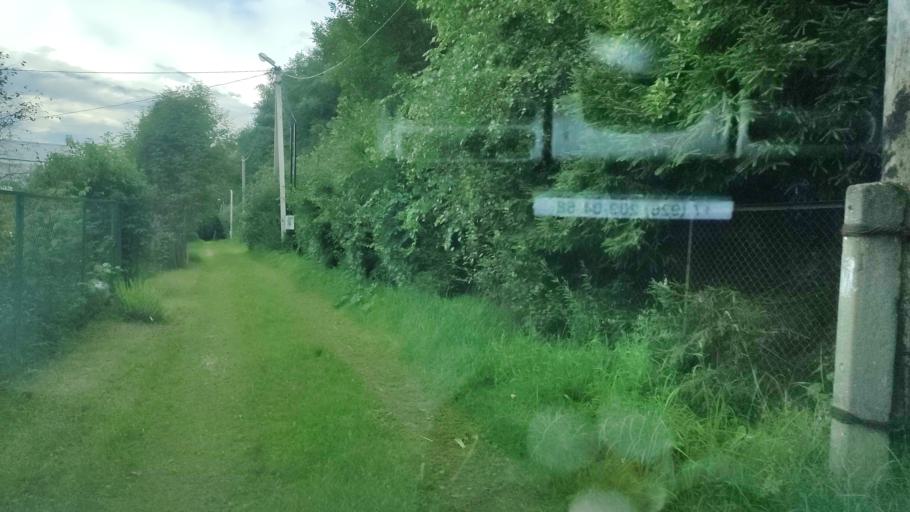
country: RU
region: Moskovskaya
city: Khot'kovo
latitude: 56.2093
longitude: 37.9779
